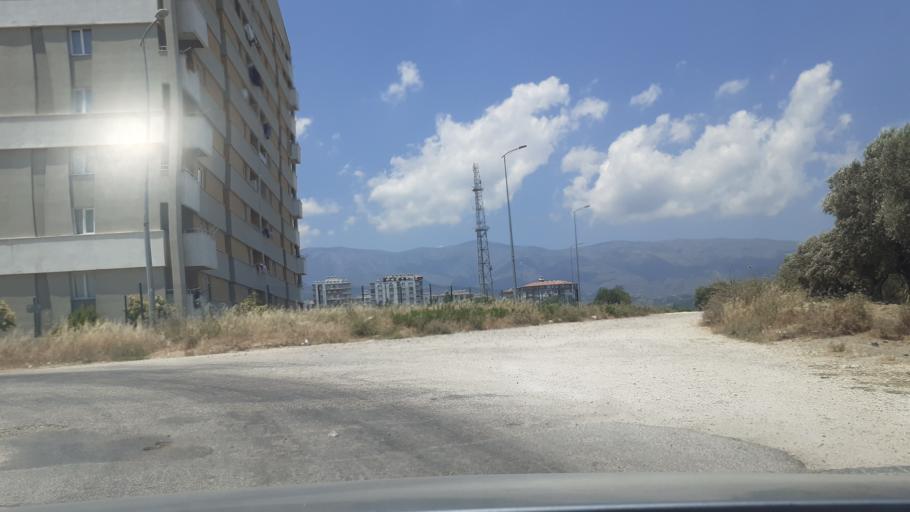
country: TR
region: Hatay
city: Gunyazi
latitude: 36.2347
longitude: 36.1386
